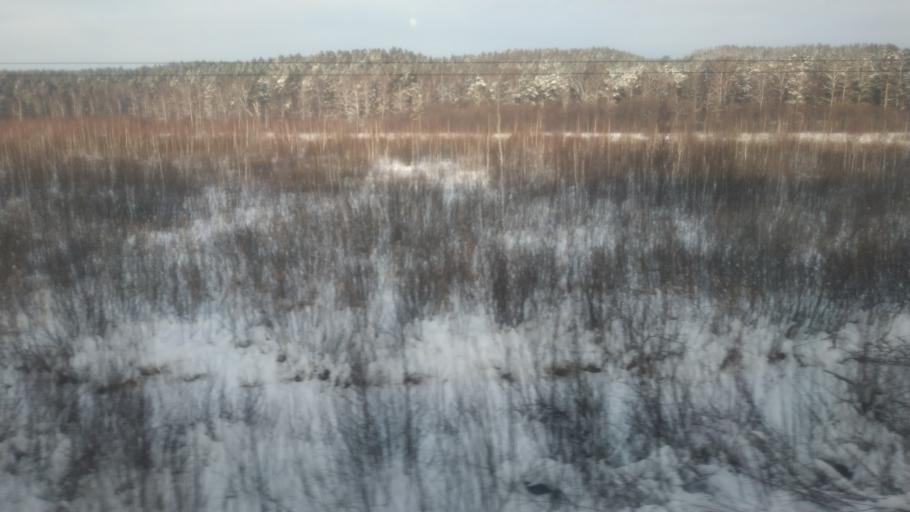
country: RU
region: Kirov
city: Krasnaya Polyana
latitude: 56.2537
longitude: 51.1364
